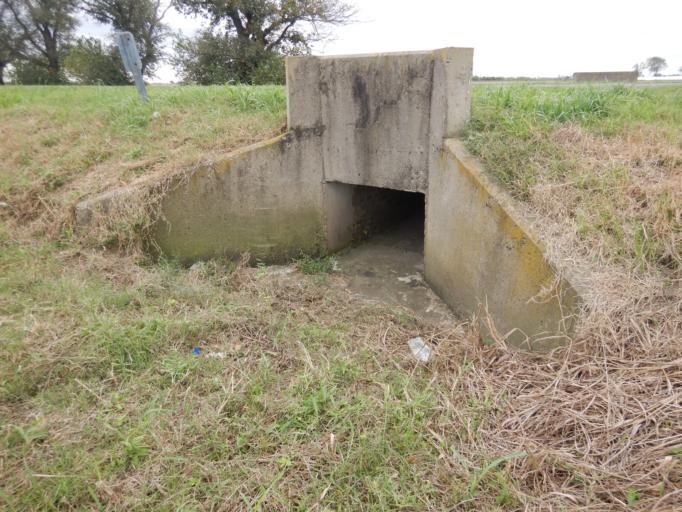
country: AR
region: Santa Fe
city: Carcarana
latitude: -32.8798
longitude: -61.0537
